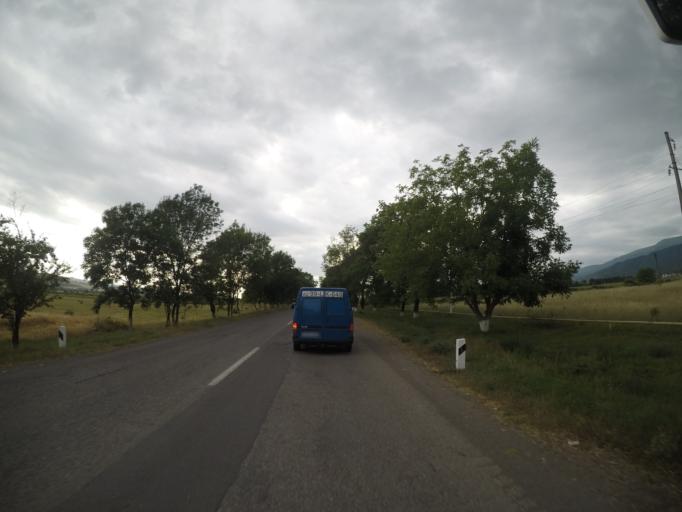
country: AZ
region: Ismayilli
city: Ismayilli
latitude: 40.7756
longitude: 48.1969
